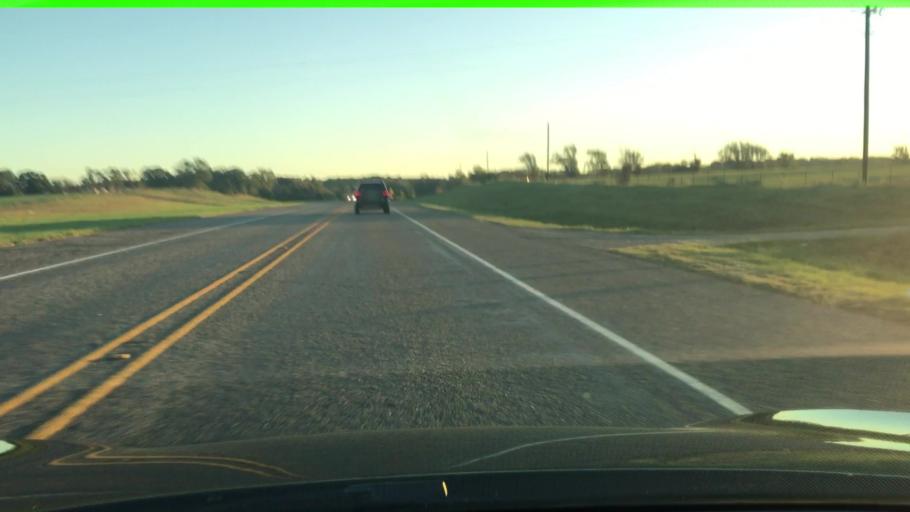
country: US
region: Texas
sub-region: Henderson County
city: Athens
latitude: 32.1746
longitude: -95.8233
